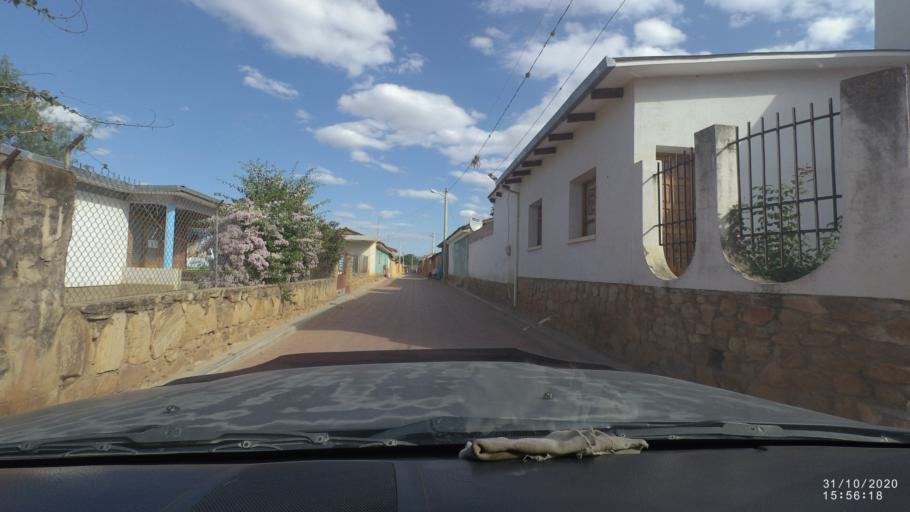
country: BO
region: Chuquisaca
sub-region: Provincia Zudanez
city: Mojocoya
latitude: -18.3221
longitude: -64.6766
